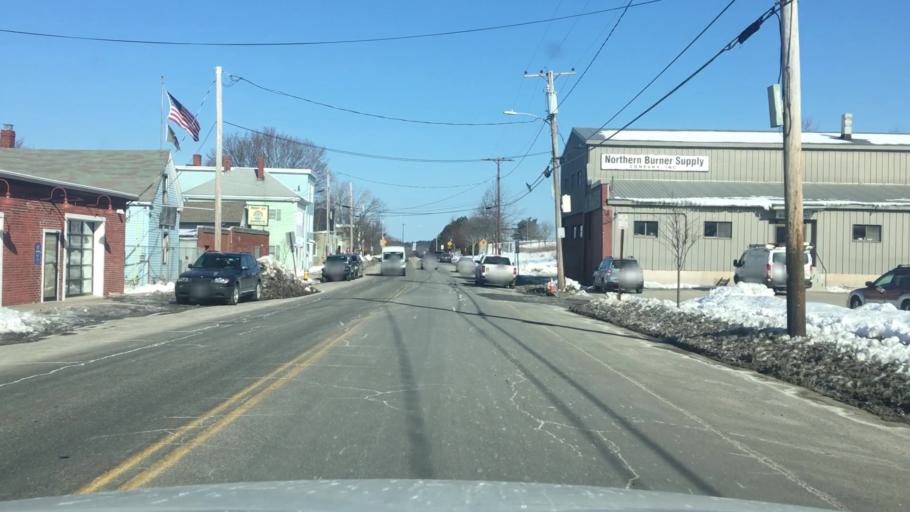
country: US
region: Maine
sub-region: Cumberland County
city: Portland
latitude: 43.6689
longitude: -70.2541
